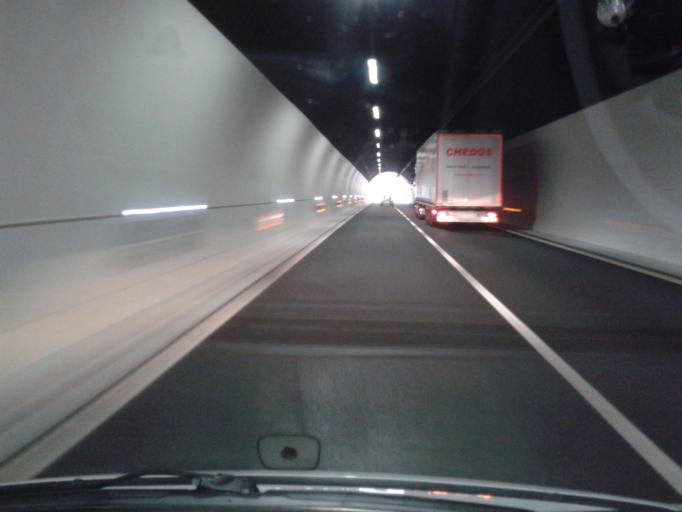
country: IT
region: Friuli Venezia Giulia
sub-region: Provincia di Udine
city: Moggio di Sotto
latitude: 46.3955
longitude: 13.1978
